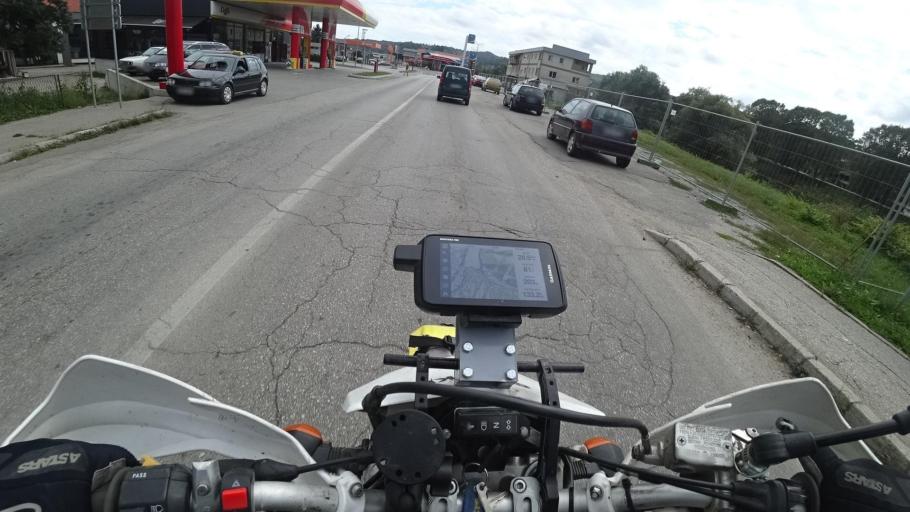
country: BA
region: Republika Srpska
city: Bosanski Novi
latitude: 45.0495
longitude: 16.3848
